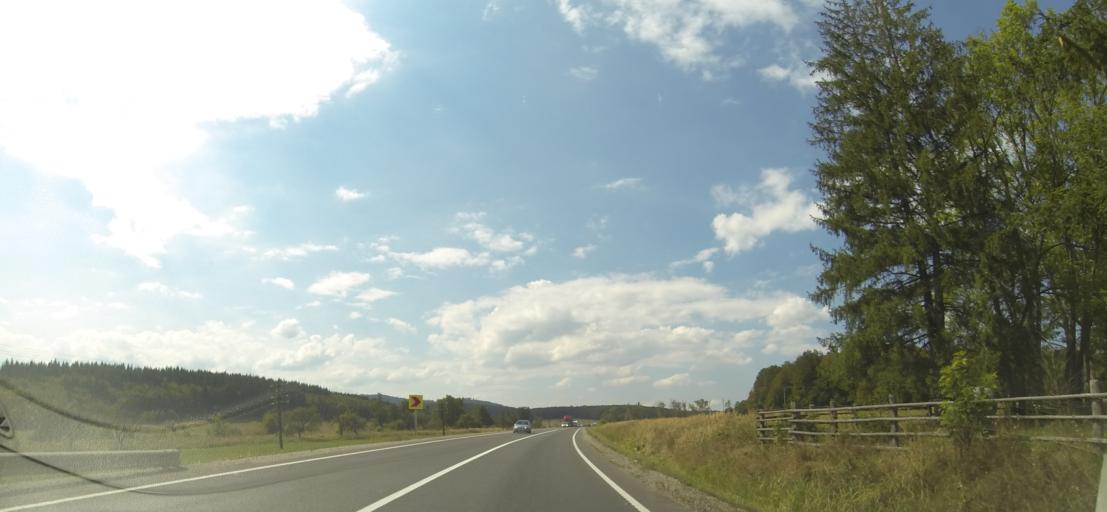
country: RO
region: Brasov
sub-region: Comuna Sinca Noua
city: Sinca Noua
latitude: 45.7444
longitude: 25.2983
